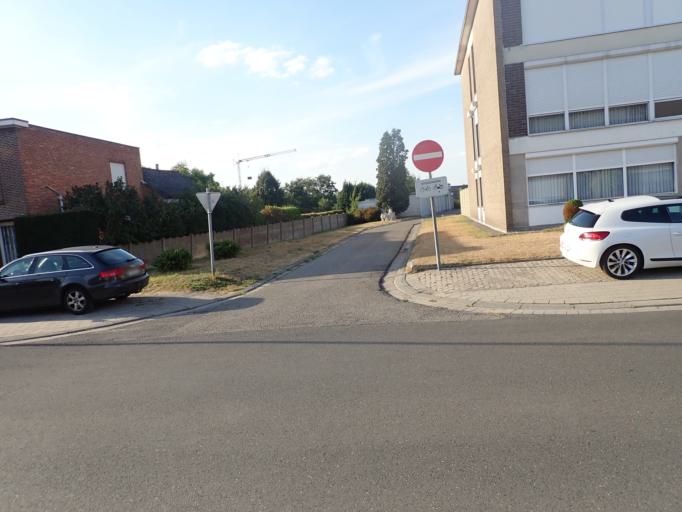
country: BE
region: Flanders
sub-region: Provincie Antwerpen
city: Berlaar
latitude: 51.1132
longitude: 4.6550
